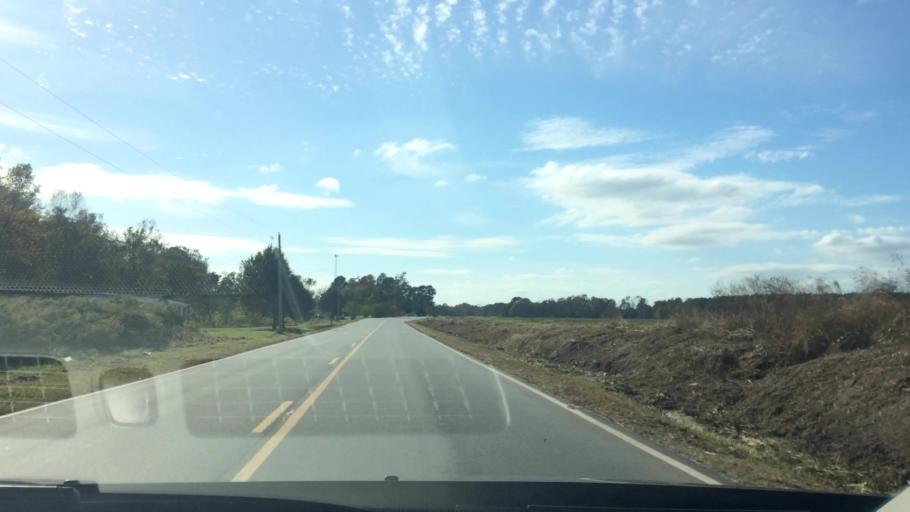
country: US
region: North Carolina
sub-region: Pitt County
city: Ayden
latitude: 35.4573
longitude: -77.4722
